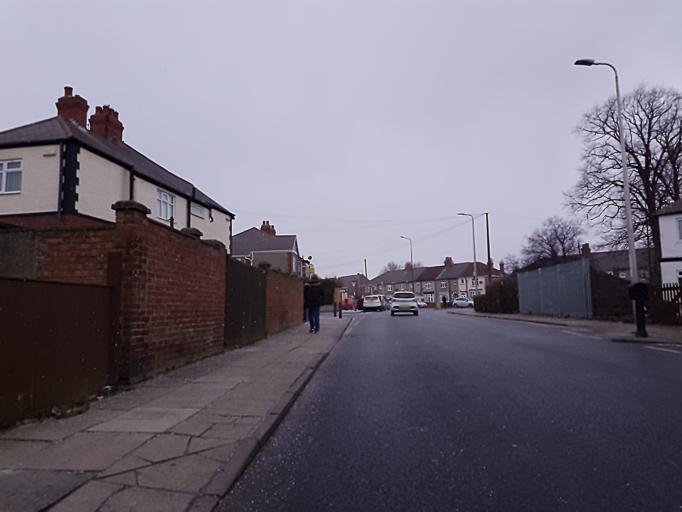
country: GB
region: England
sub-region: North East Lincolnshire
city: Grimbsy
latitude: 53.5624
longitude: -0.1095
